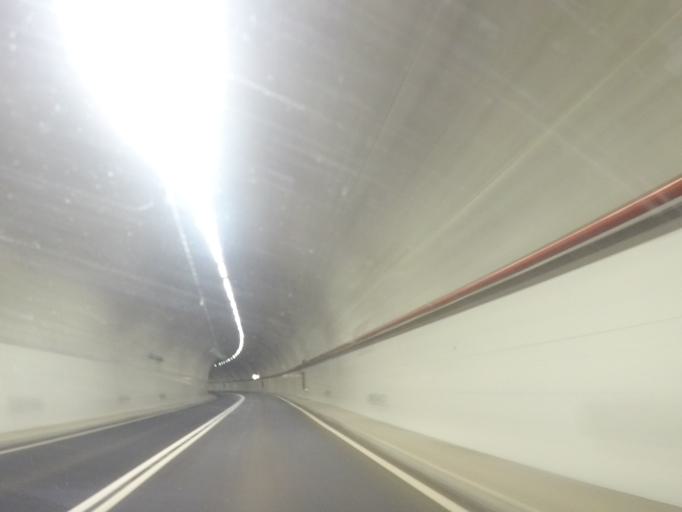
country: PT
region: Madeira
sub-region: Calheta
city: Faja da Ovelha
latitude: 32.7857
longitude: -17.2279
